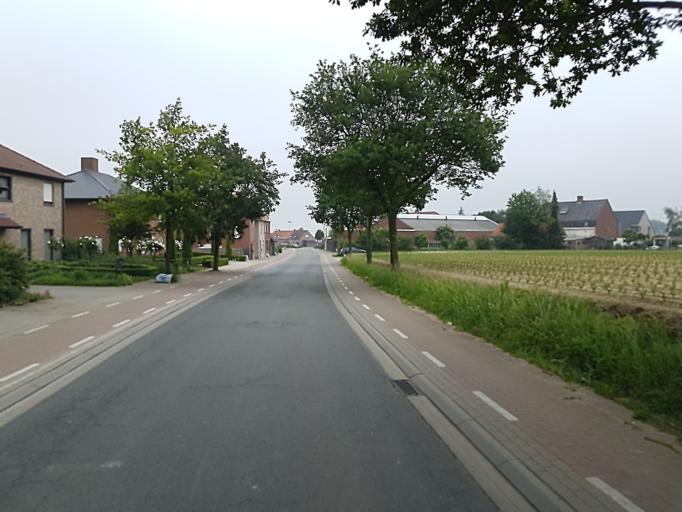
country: BE
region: Flanders
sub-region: Provincie West-Vlaanderen
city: Moorslede
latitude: 50.9012
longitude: 3.0676
